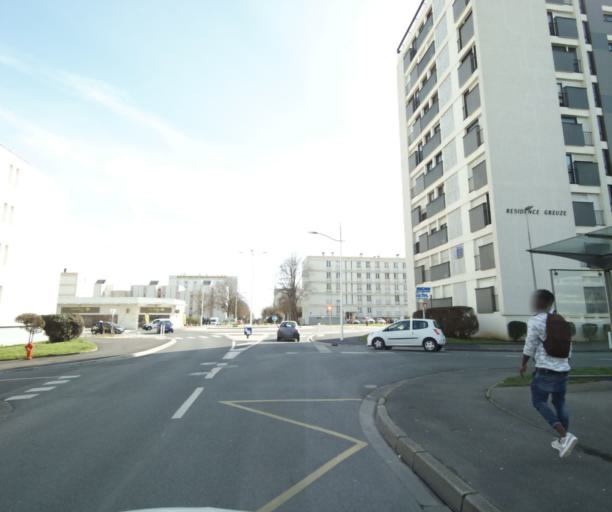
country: FR
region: Poitou-Charentes
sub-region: Departement de la Charente-Maritime
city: La Rochelle
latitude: 46.1694
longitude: -1.1723
